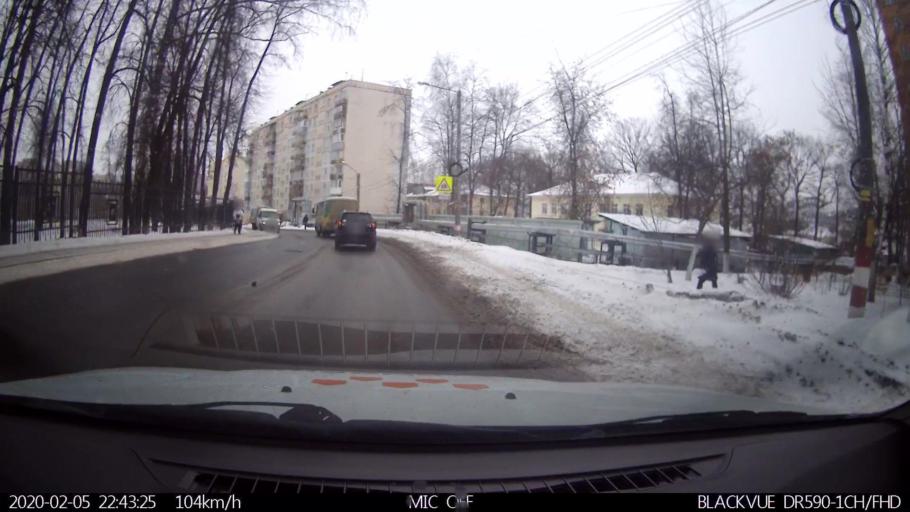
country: RU
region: Nizjnij Novgorod
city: Imeni Stepana Razina
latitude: 54.7126
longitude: 44.3767
